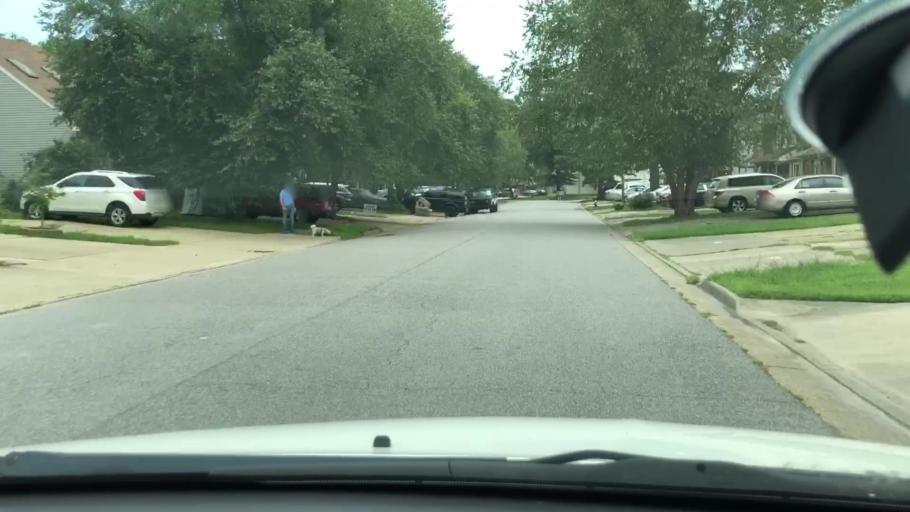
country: US
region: Virginia
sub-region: City of Virginia Beach
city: Virginia Beach
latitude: 36.8438
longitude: -76.1139
